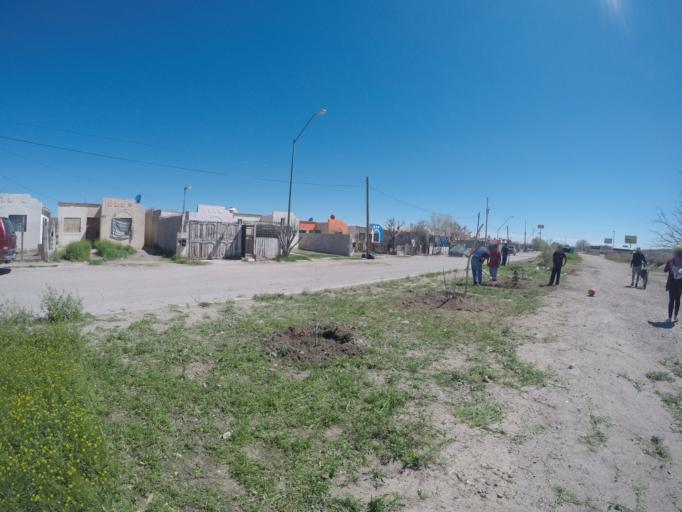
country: US
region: Texas
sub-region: El Paso County
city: Socorro Mission Number 1 Colonia
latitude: 31.6051
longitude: -106.3101
